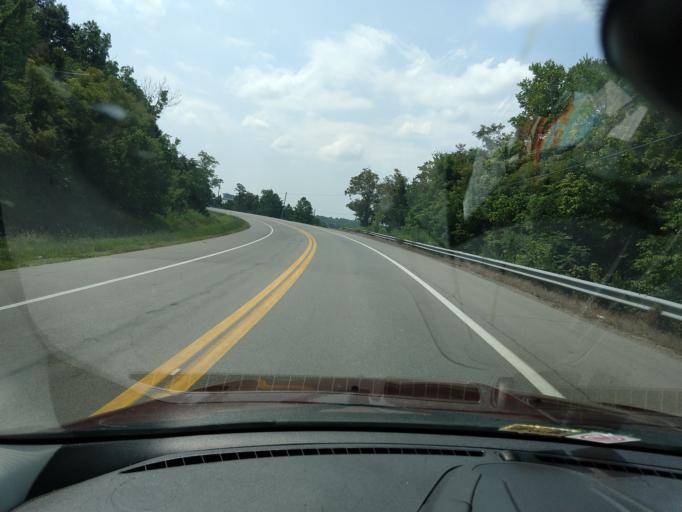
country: US
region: West Virginia
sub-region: Jackson County
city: Ravenswood
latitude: 38.8622
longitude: -81.8193
